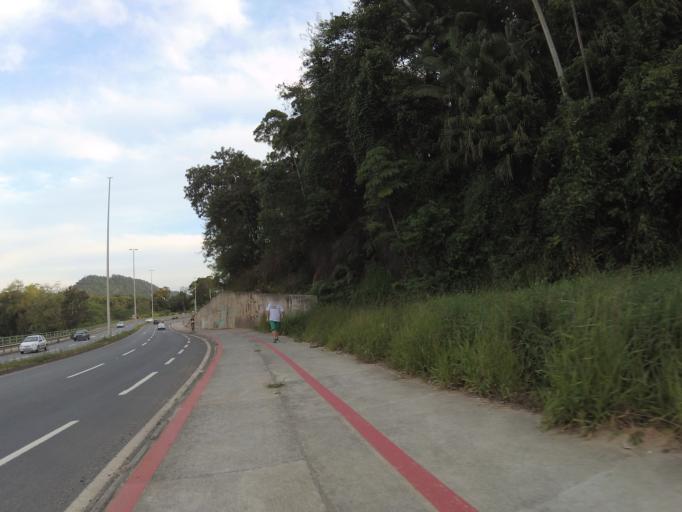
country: BR
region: Santa Catarina
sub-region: Blumenau
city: Blumenau
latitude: -26.8879
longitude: -49.1409
